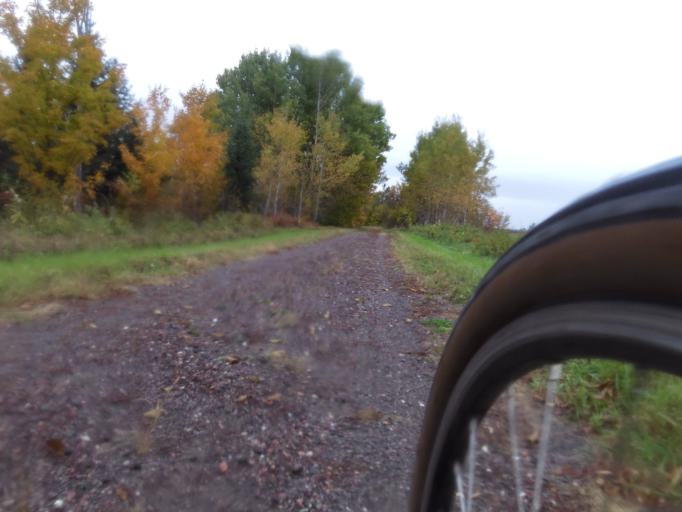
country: CA
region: Quebec
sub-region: Outaouais
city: Shawville
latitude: 45.6400
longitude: -76.5190
